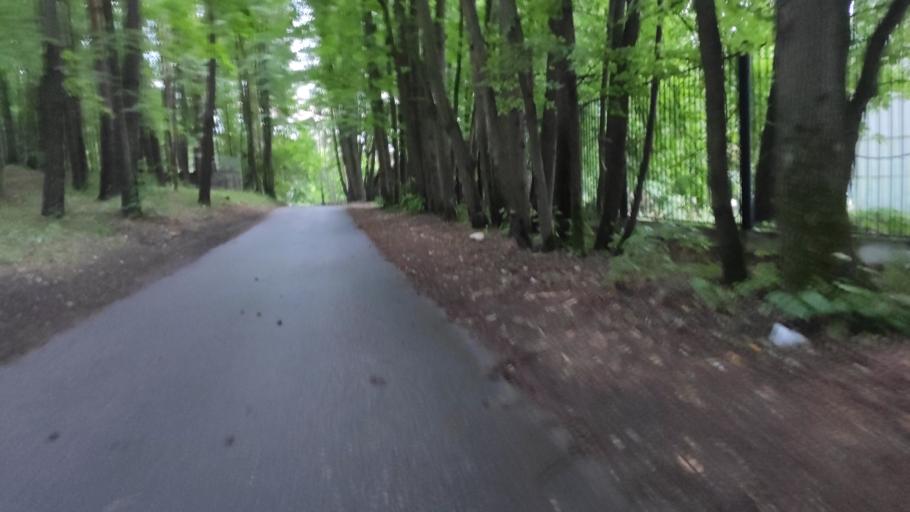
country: BY
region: Minsk
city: Zhdanovichy
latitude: 53.9676
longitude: 27.4330
